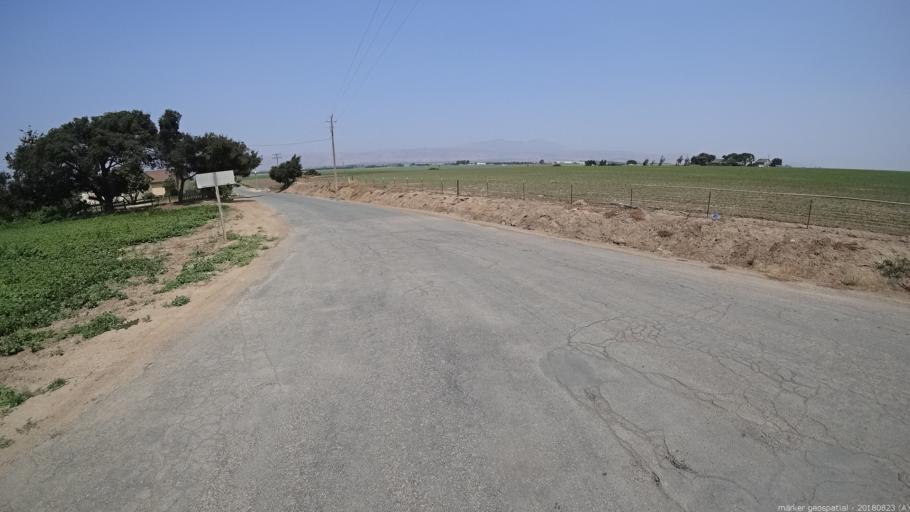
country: US
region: California
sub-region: Monterey County
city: Soledad
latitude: 36.3783
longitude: -121.3404
